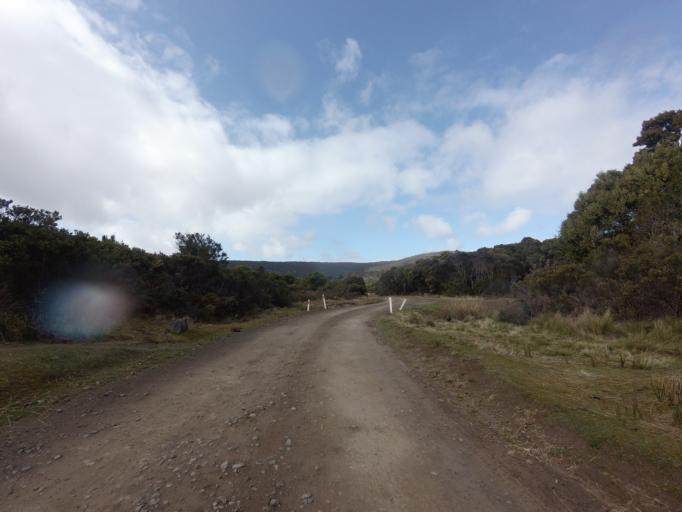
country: AU
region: Tasmania
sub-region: Huon Valley
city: Geeveston
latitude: -43.5788
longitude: 146.8870
